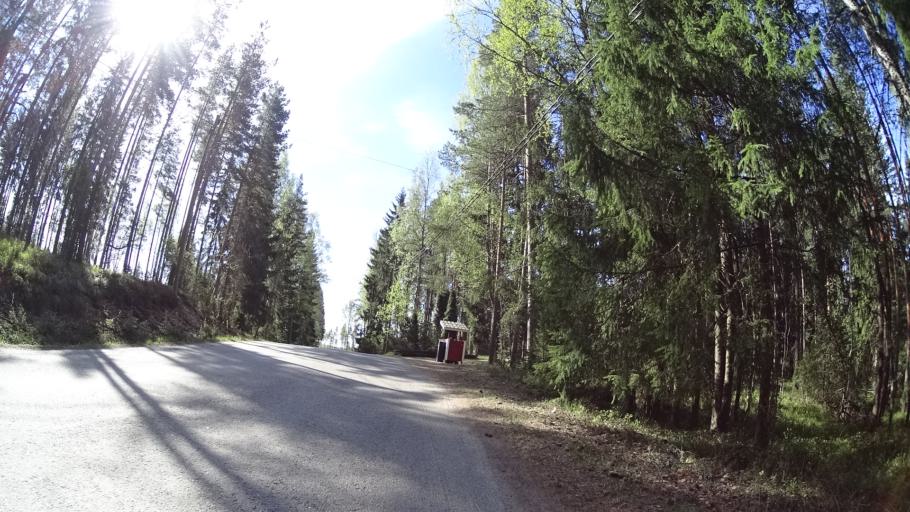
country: FI
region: Uusimaa
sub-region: Helsinki
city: Nurmijaervi
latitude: 60.4491
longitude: 24.8244
